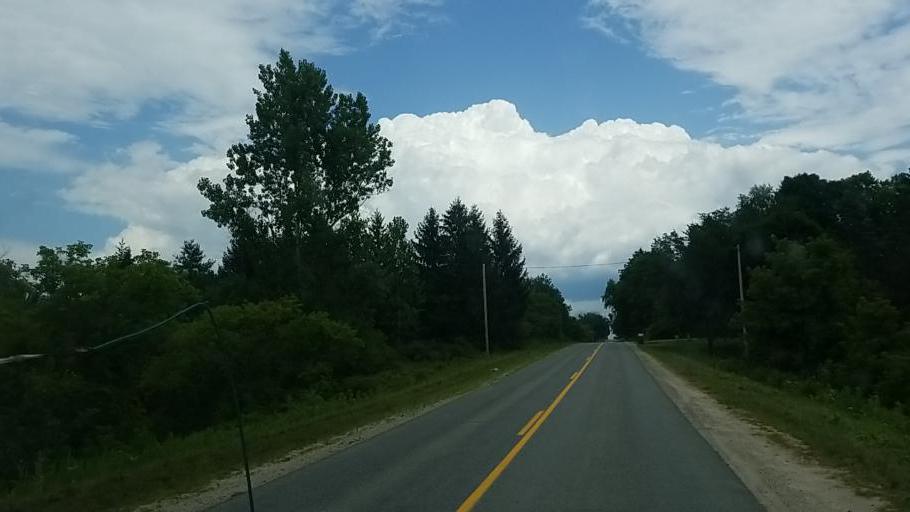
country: US
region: Michigan
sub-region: Kent County
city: Walker
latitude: 43.0163
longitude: -85.8058
